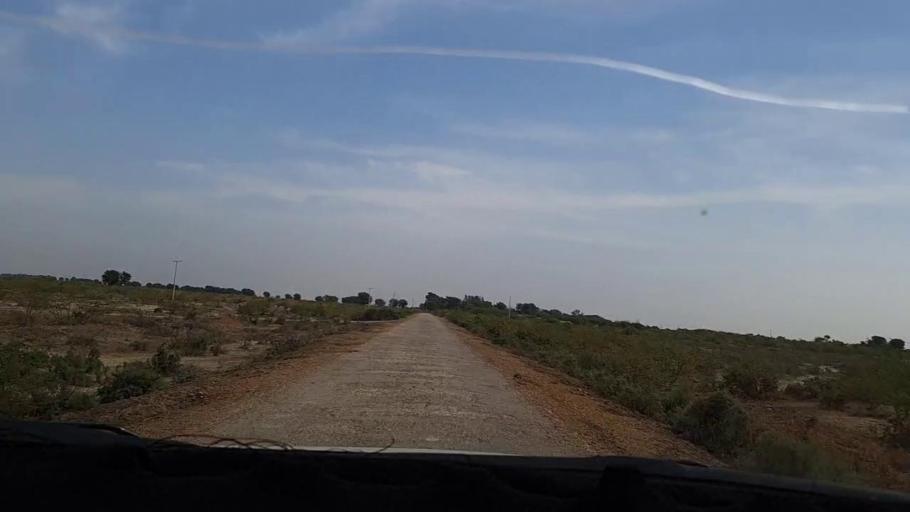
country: PK
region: Sindh
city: Pithoro
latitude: 25.5374
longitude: 69.3365
